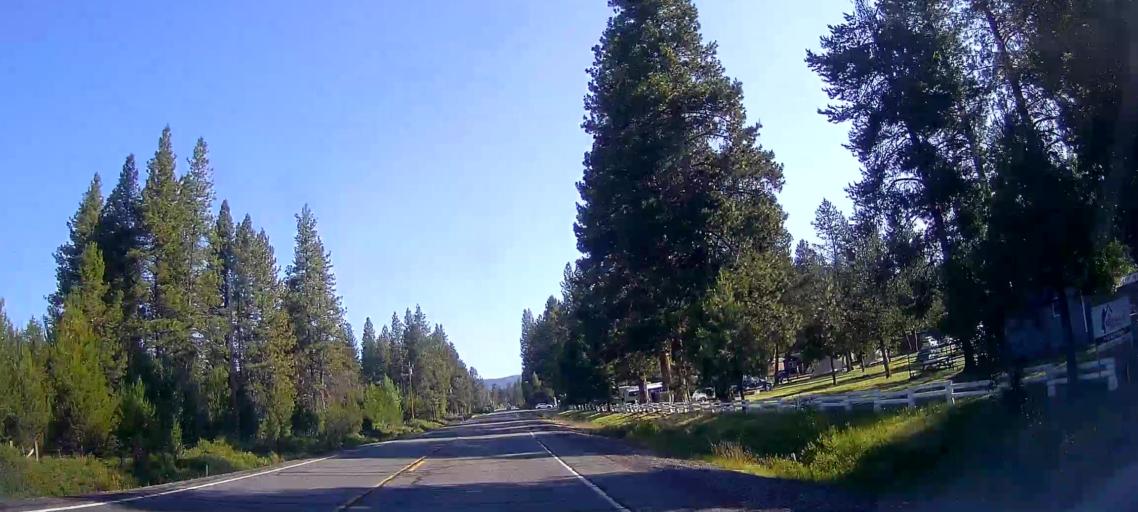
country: US
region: Oregon
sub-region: Klamath County
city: Klamath Falls
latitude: 42.6834
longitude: -121.9735
